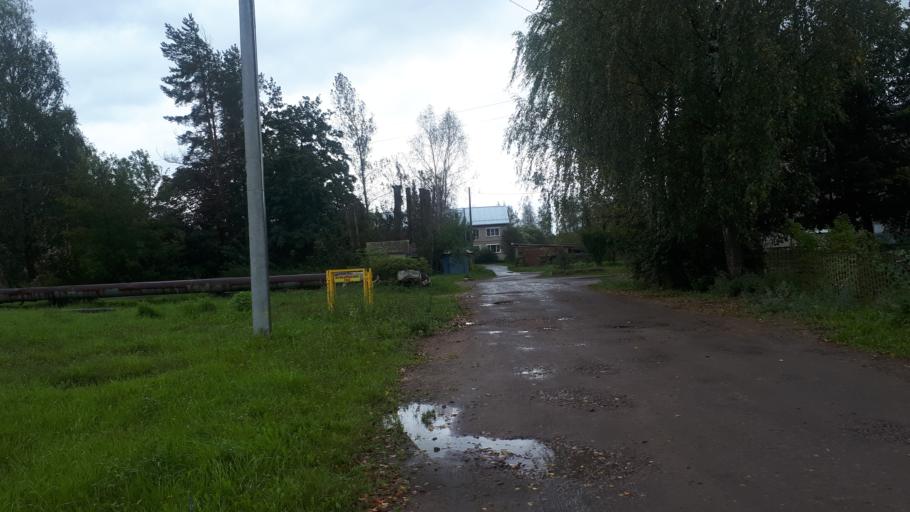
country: RU
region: Jaroslavl
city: Konstantinovskiy
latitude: 57.8283
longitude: 39.5874
